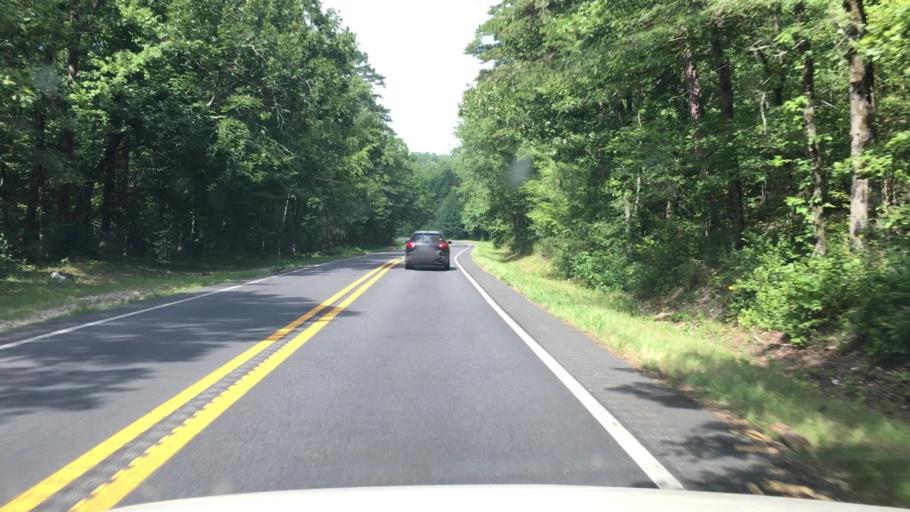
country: US
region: Arkansas
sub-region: Garland County
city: Lake Hamilton
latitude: 34.3603
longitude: -93.1732
